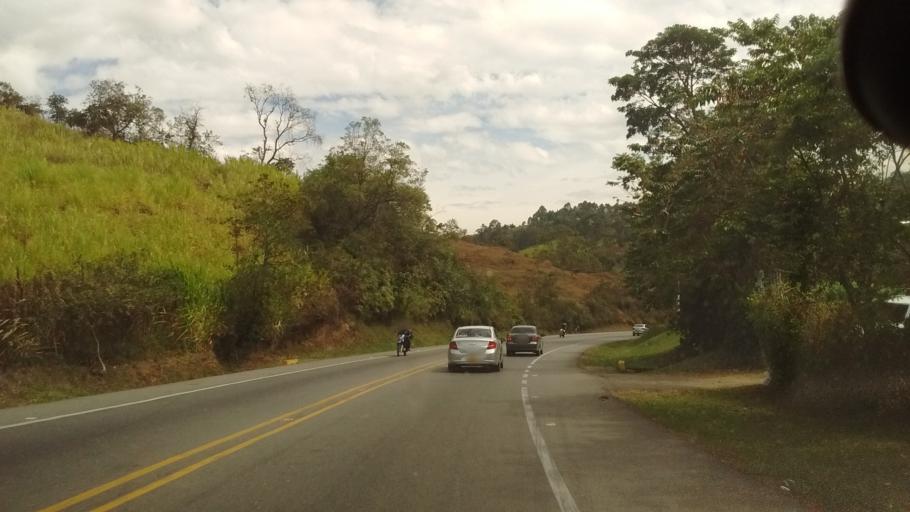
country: CO
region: Cauca
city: Cajibio
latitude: 2.6066
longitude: -76.5287
